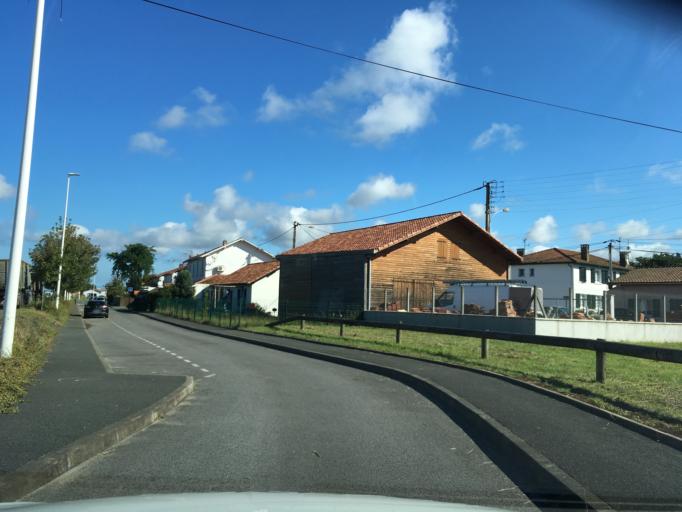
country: FR
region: Aquitaine
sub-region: Departement des Pyrenees-Atlantiques
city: Bayonne
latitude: 43.5060
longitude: -1.4873
